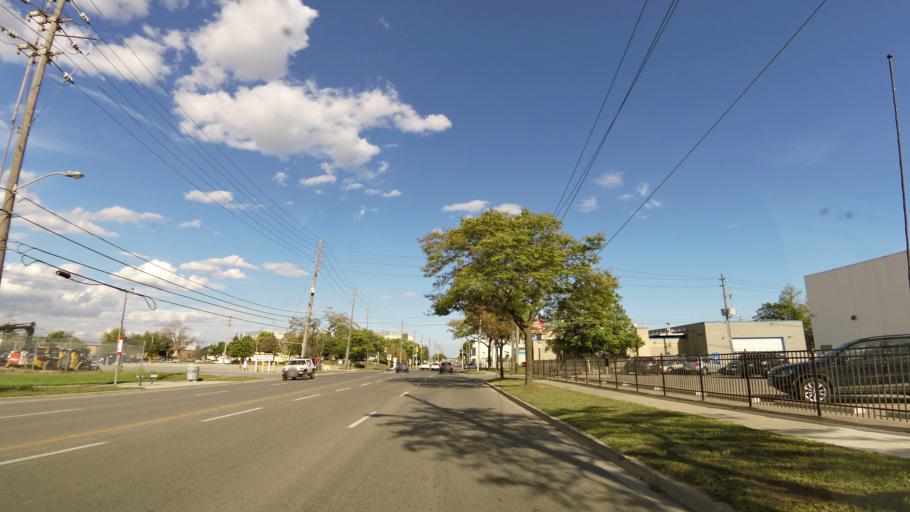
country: CA
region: Ontario
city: Etobicoke
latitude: 43.6068
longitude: -79.5225
